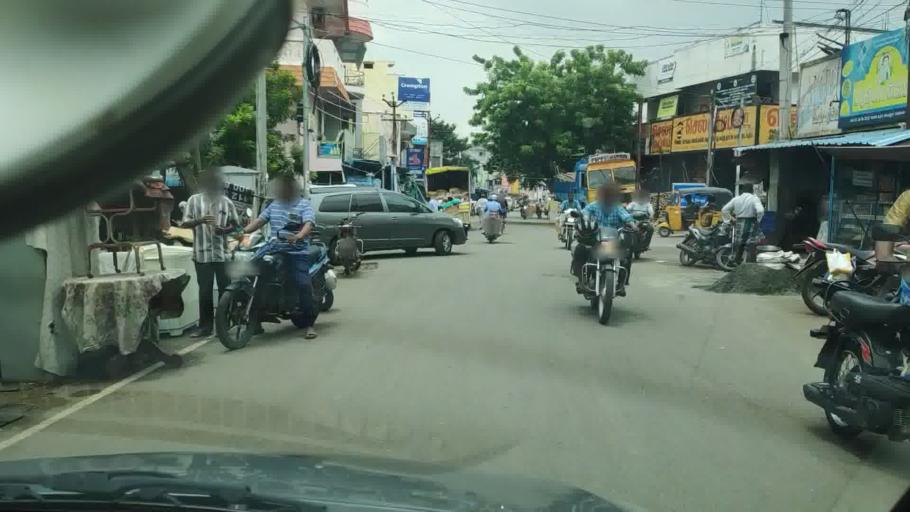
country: IN
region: Tamil Nadu
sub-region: Thiruvallur
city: Ambattur
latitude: 13.1188
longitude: 80.1575
